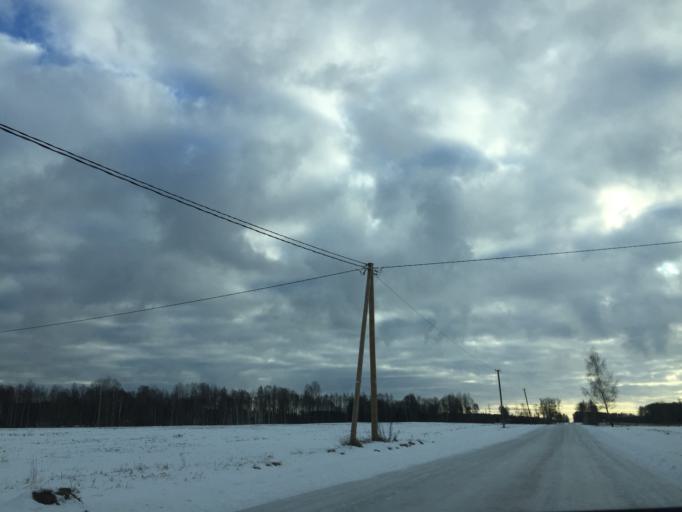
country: LV
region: Lielvarde
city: Lielvarde
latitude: 56.5595
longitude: 24.7355
